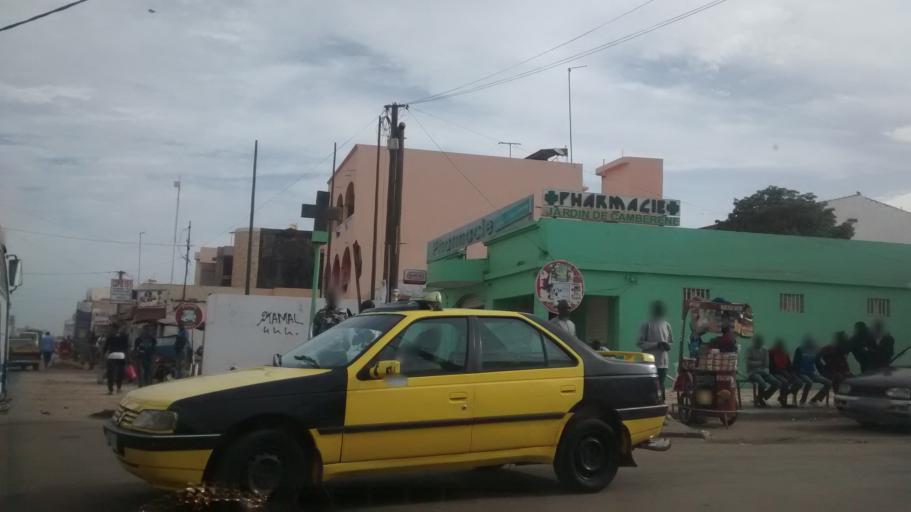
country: SN
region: Dakar
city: Pikine
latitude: 14.7574
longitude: -17.4283
